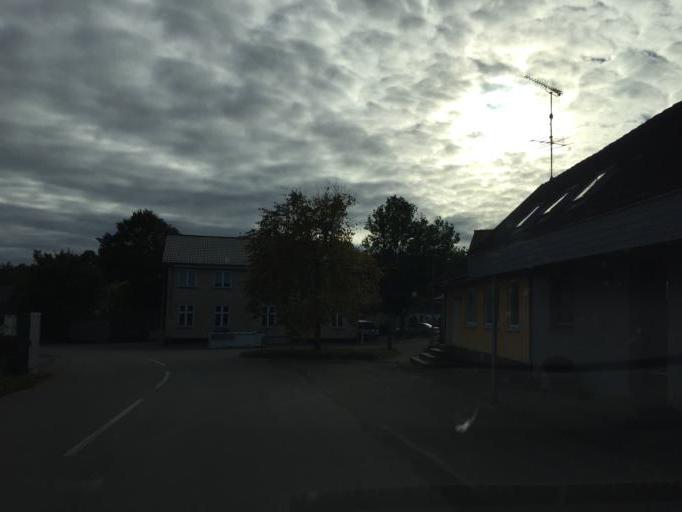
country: DK
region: Zealand
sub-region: Odsherred Kommune
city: Asnaes
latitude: 55.8290
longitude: 11.4550
